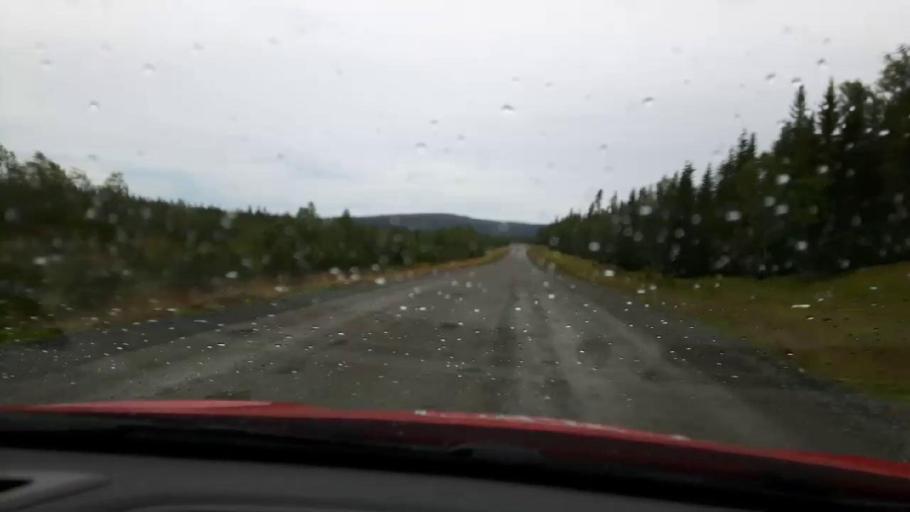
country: NO
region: Nord-Trondelag
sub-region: Meraker
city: Meraker
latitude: 63.5593
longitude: 12.3057
